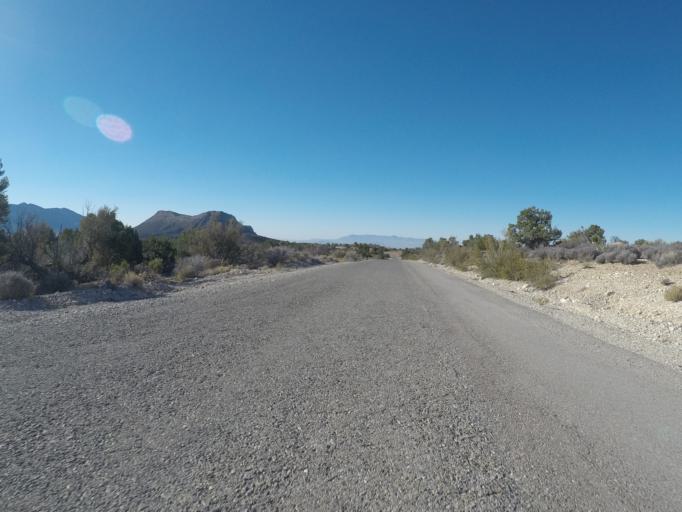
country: US
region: Nevada
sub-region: Clark County
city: Summerlin South
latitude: 36.0805
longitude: -115.5621
